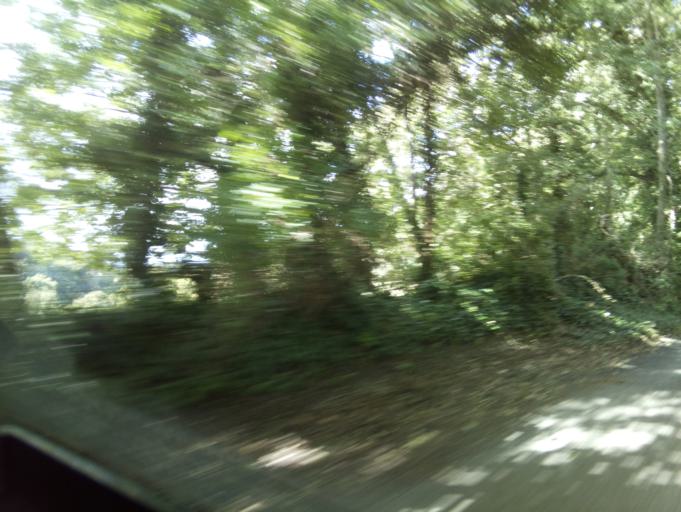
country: GB
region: England
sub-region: Wiltshire
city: Erlestoke
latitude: 51.2829
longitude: -2.0671
